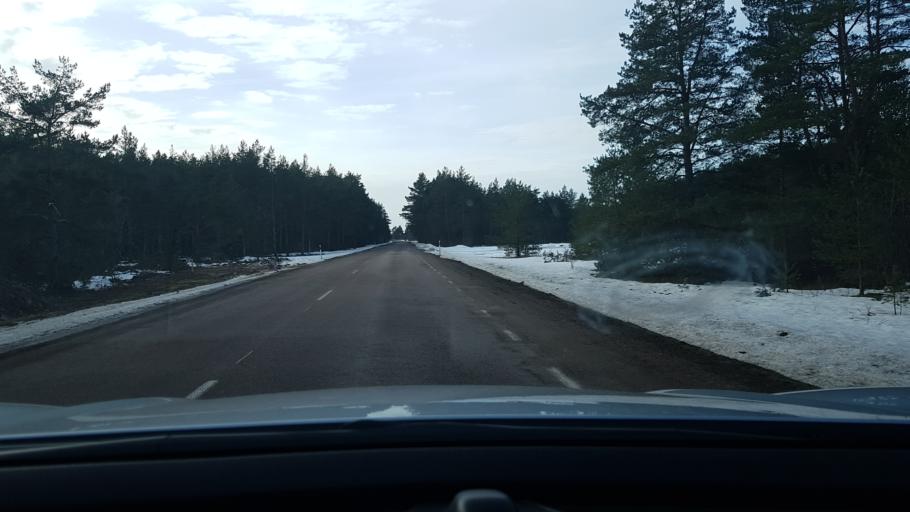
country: EE
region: Saare
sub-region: Kuressaare linn
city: Kuressaare
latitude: 58.3432
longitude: 22.5808
